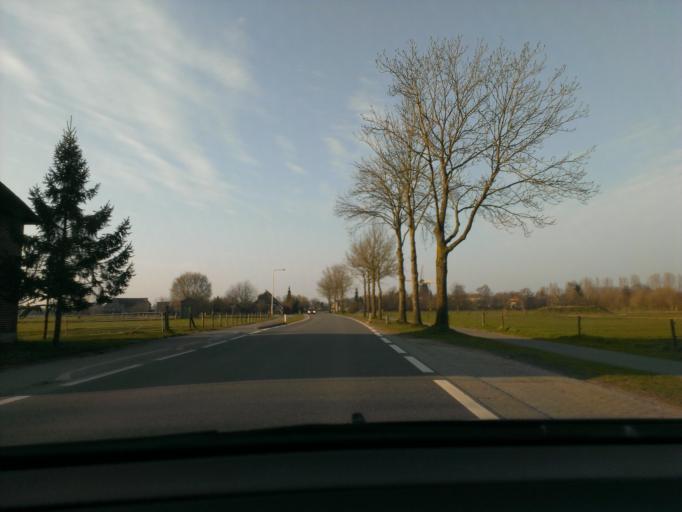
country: NL
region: Gelderland
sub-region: Gemeente Voorst
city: Twello
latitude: 52.2682
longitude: 6.1064
